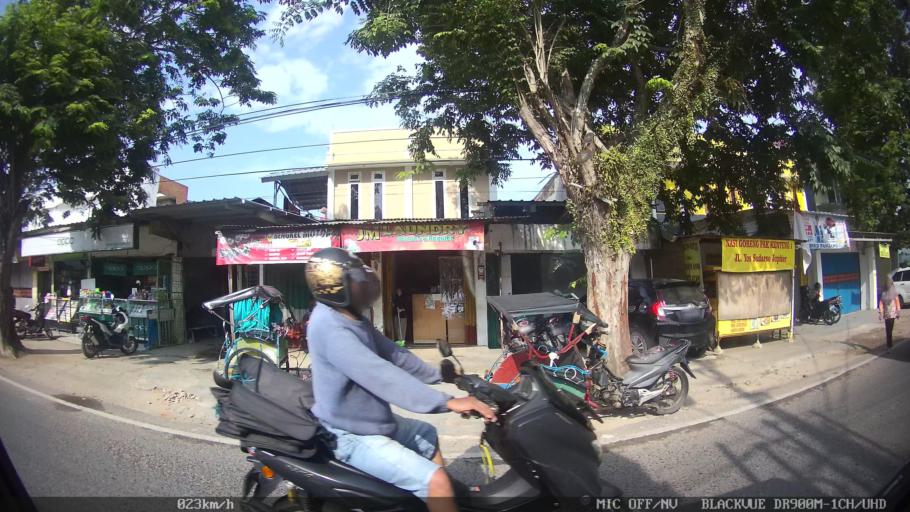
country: ID
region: Lampung
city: Panjang
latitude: -5.4765
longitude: 105.3222
